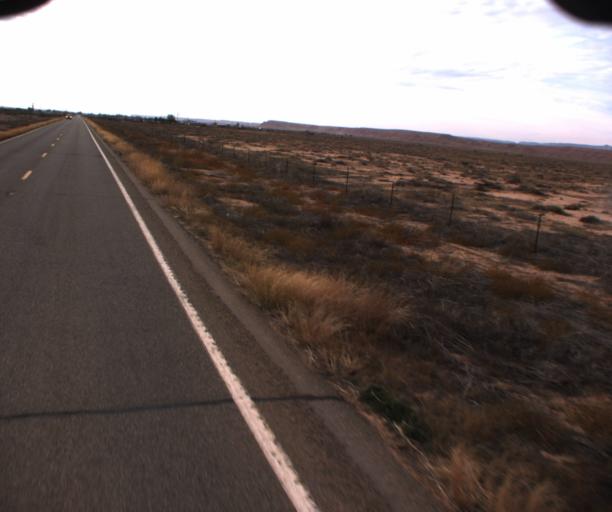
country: US
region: Arizona
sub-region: Apache County
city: Many Farms
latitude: 36.4437
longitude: -109.6075
